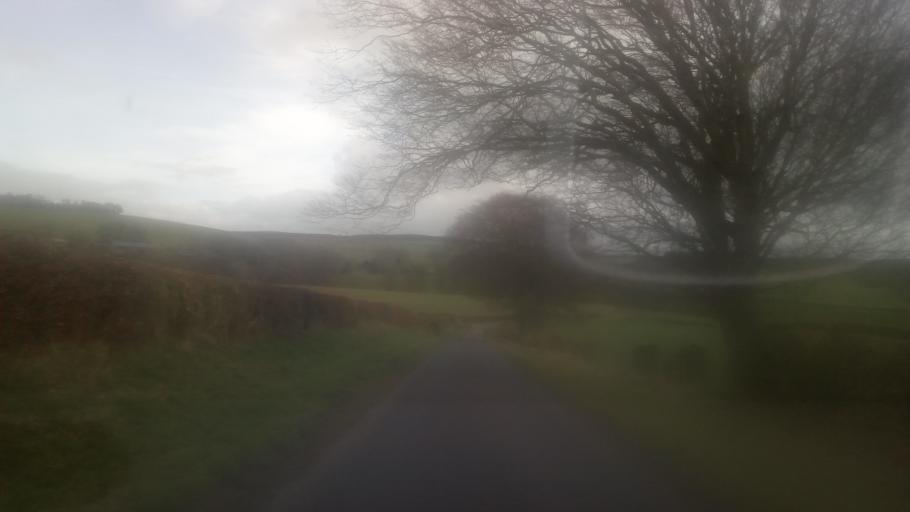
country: GB
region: Scotland
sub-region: The Scottish Borders
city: Jedburgh
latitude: 55.4891
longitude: -2.4896
